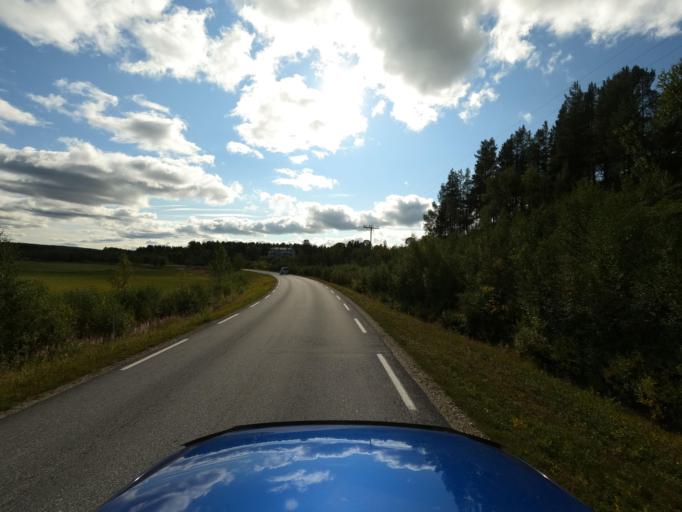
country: NO
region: Finnmark Fylke
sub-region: Karasjok
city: Karasjohka
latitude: 69.4028
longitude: 25.8116
